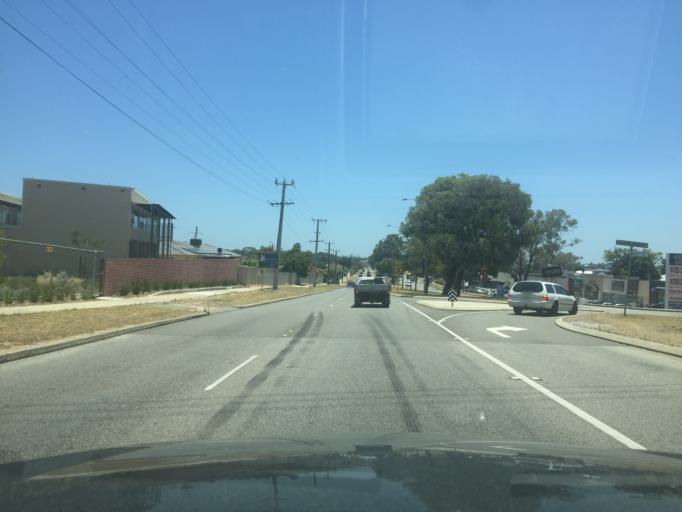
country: AU
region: Western Australia
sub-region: Fremantle
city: Samson
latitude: -32.0660
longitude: 115.8034
